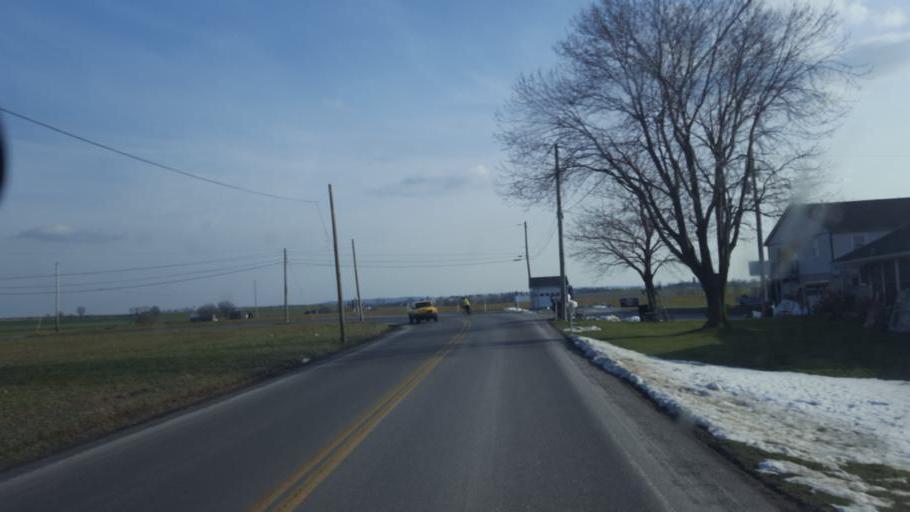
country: US
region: Pennsylvania
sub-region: Lancaster County
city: Intercourse
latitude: 40.0541
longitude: -76.1345
